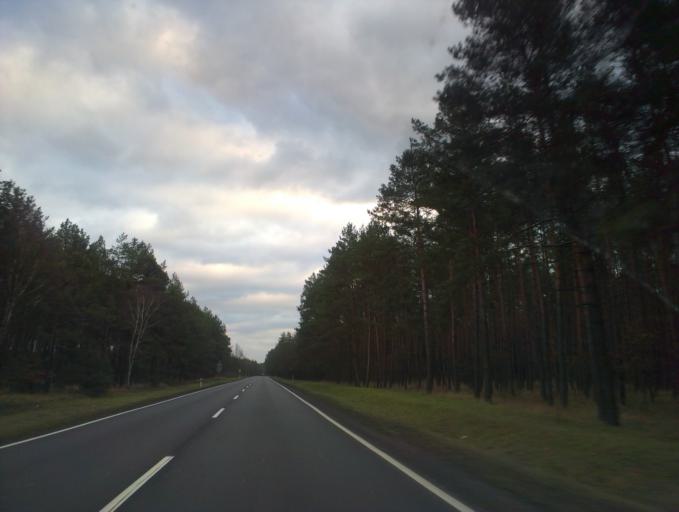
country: PL
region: Greater Poland Voivodeship
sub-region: Powiat pilski
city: Pila
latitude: 53.1897
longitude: 16.7653
